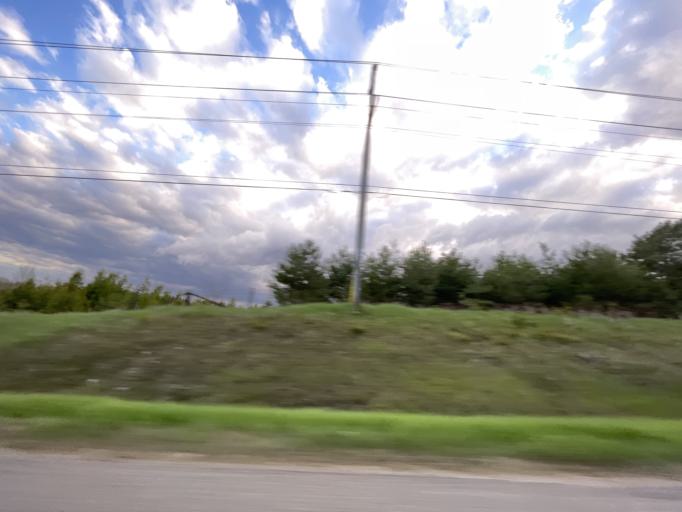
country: CA
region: Ontario
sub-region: Wellington County
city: Guelph
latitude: 43.5917
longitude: -80.2793
